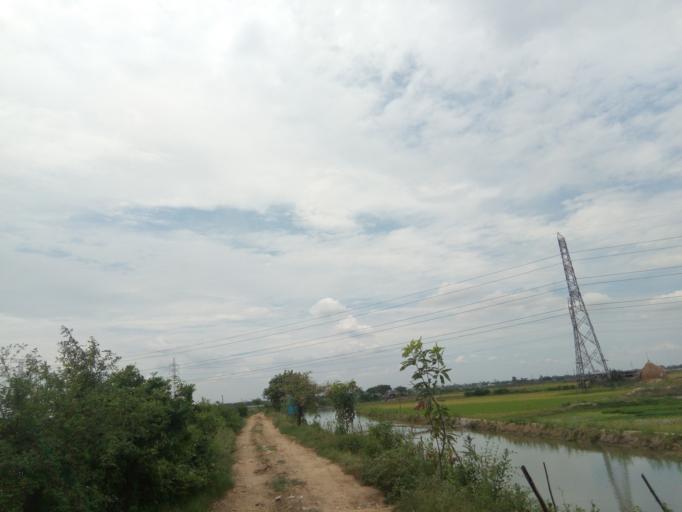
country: BD
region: Dhaka
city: Paltan
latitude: 23.7227
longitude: 90.4629
